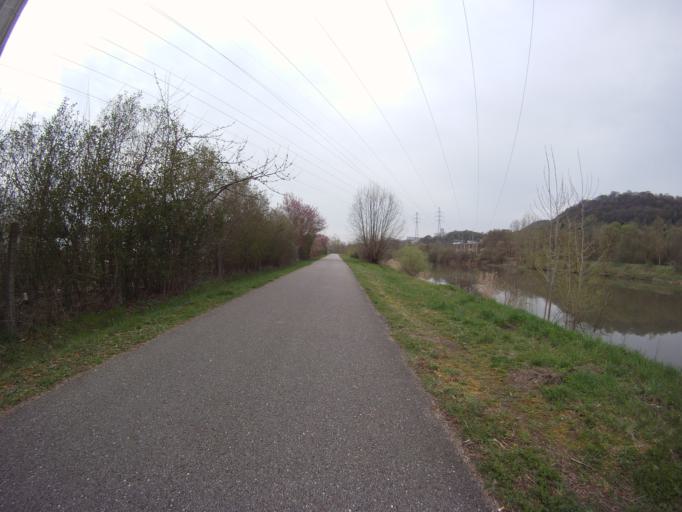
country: FR
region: Lorraine
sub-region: Departement de Meurthe-et-Moselle
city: Champigneulles
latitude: 48.7261
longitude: 6.1758
